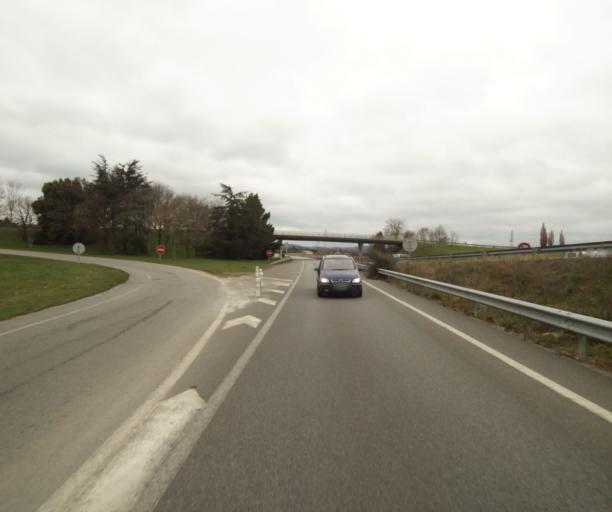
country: FR
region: Midi-Pyrenees
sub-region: Departement de l'Ariege
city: Pamiers
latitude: 43.1336
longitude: 1.6253
